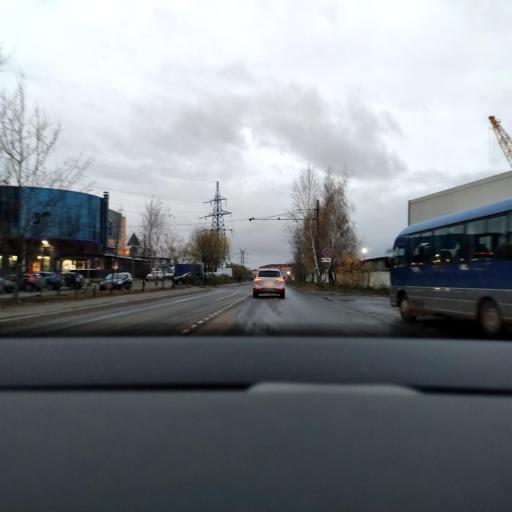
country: RU
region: Moskovskaya
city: Reutov
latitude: 55.7709
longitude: 37.8657
